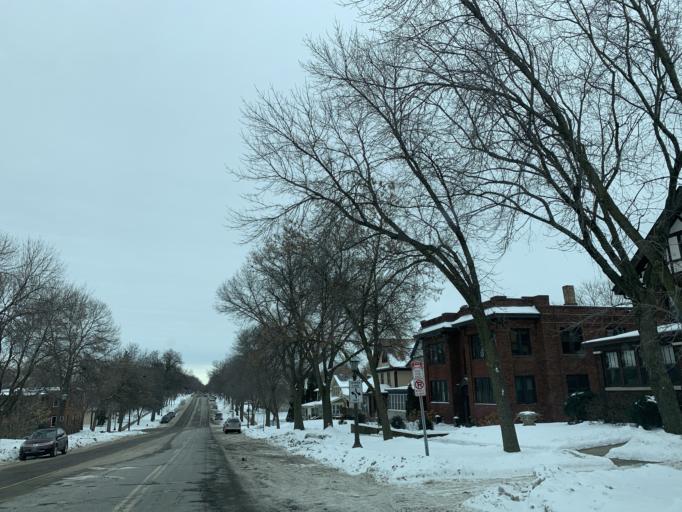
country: US
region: Minnesota
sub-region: Ramsey County
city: Falcon Heights
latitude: 44.9485
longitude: -93.1457
